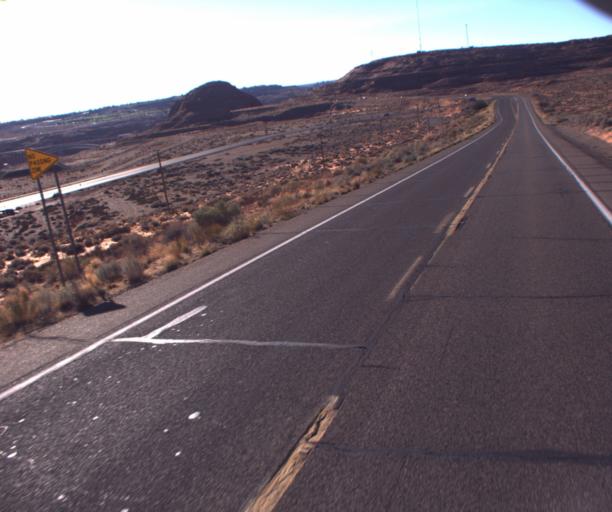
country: US
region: Arizona
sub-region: Coconino County
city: Page
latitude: 36.9442
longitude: -111.4959
